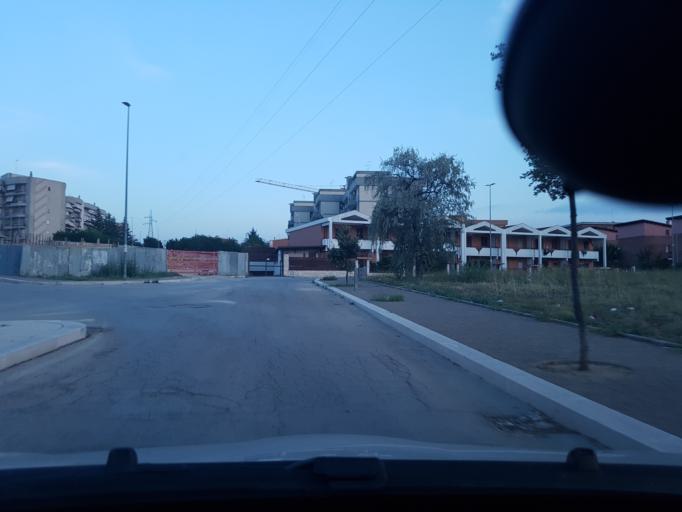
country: IT
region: Apulia
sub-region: Provincia di Foggia
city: Cerignola
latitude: 41.2629
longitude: 15.8768
